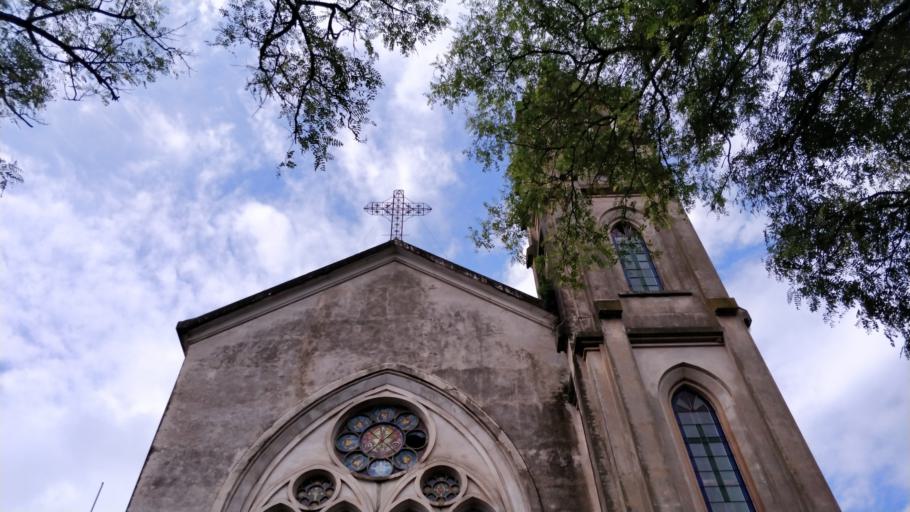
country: BR
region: Rio Grande do Sul
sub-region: Itaqui
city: Itaqui
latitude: -29.1225
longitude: -56.5564
